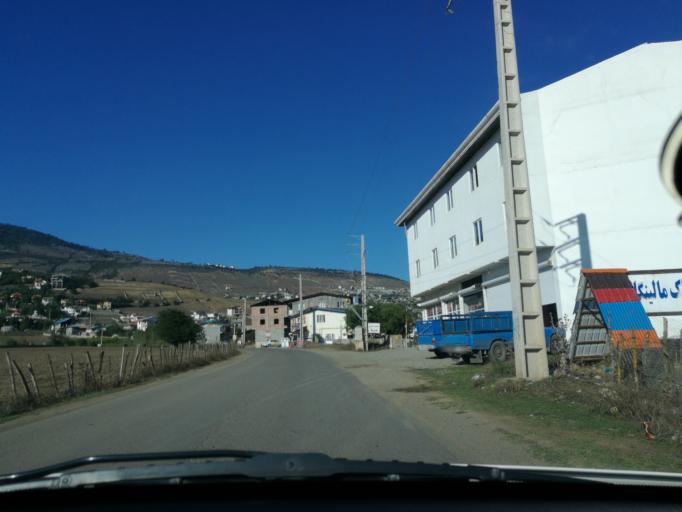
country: IR
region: Mazandaran
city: `Abbasabad
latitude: 36.5446
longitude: 51.1840
